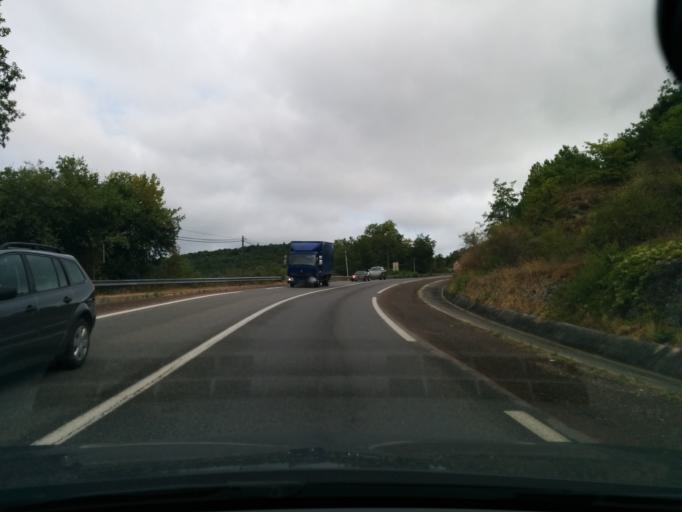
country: FR
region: Midi-Pyrenees
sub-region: Departement du Lot
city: Cahors
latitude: 44.4703
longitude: 1.4299
